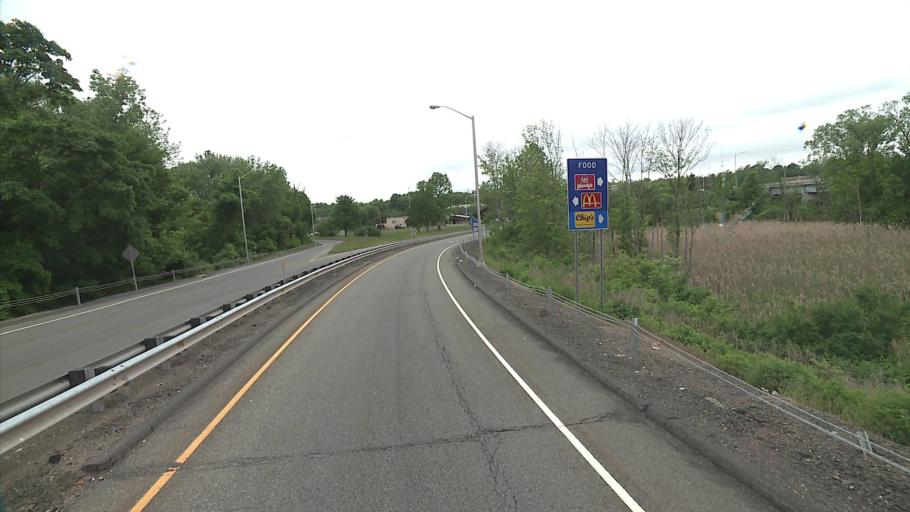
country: US
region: Connecticut
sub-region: Hartford County
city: Wethersfield
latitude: 41.6805
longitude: -72.6518
